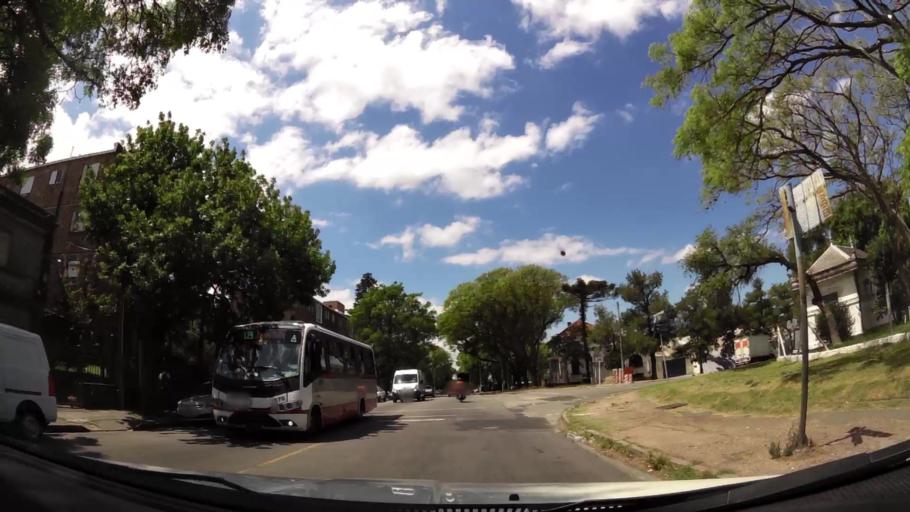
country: UY
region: Montevideo
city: Montevideo
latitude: -34.8542
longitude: -56.2096
